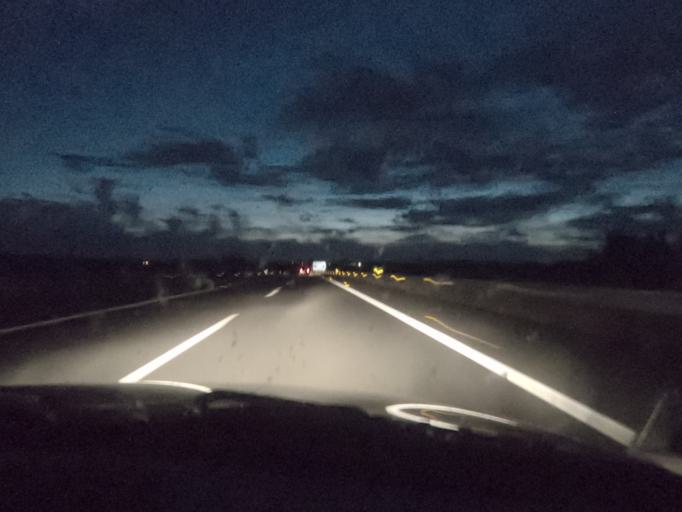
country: ES
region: Extremadura
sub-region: Provincia de Caceres
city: Morcillo
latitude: 39.9813
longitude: -6.4017
